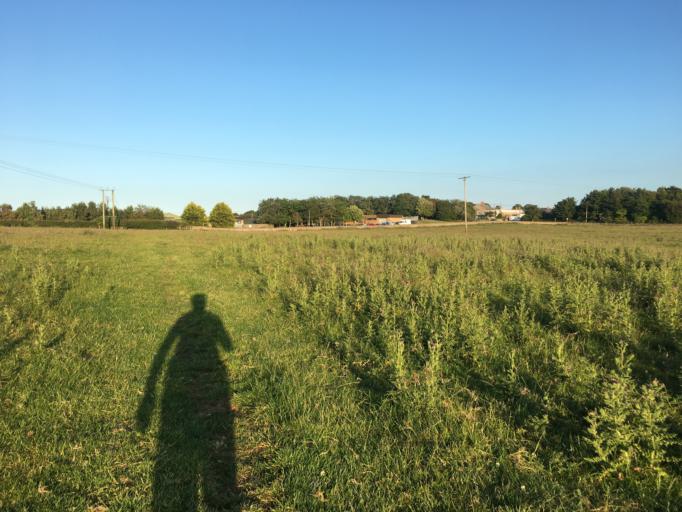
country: GB
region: England
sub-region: Northumberland
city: North Sunderland
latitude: 55.5797
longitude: -1.6703
